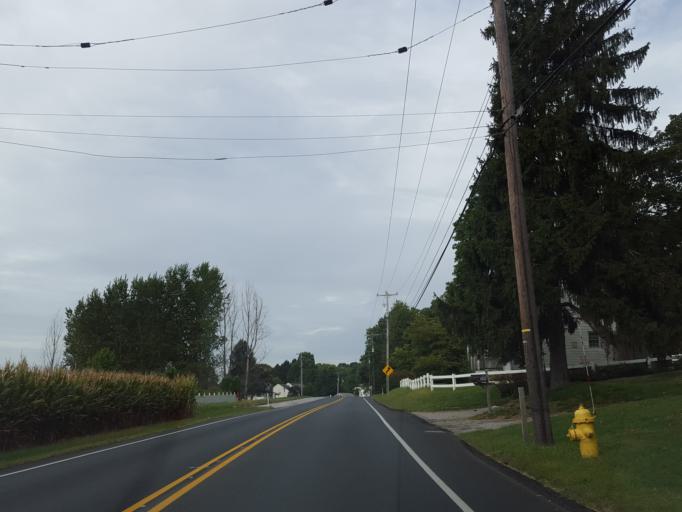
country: US
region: Pennsylvania
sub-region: York County
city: Spry
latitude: 39.9096
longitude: -76.6885
